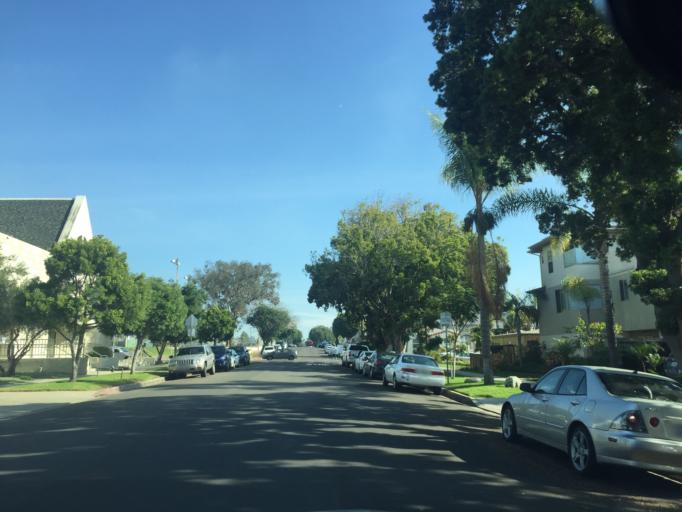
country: US
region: California
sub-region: San Diego County
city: La Jolla
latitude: 32.7997
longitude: -117.2456
